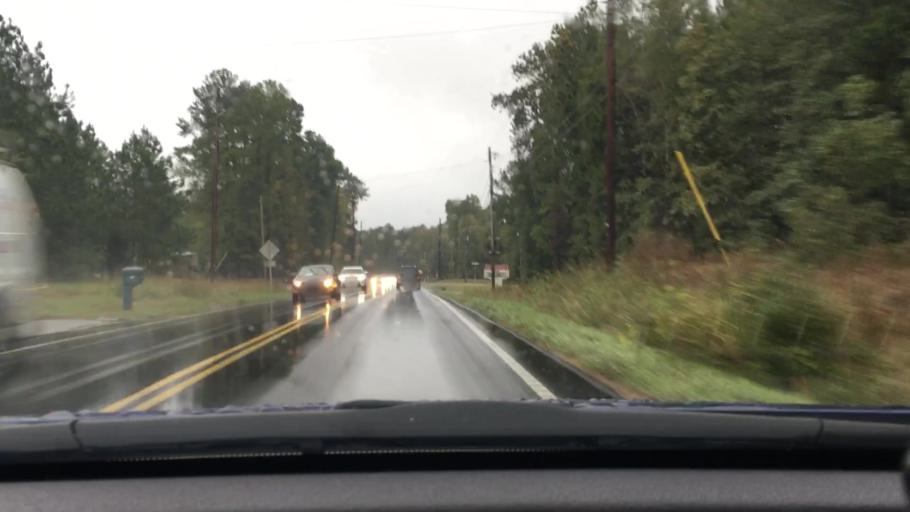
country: US
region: South Carolina
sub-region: Lexington County
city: Irmo
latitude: 34.1019
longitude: -81.1603
